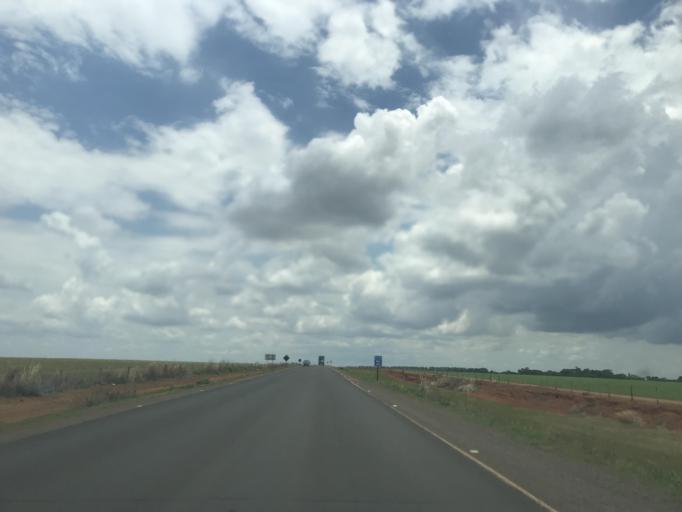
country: BR
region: Goias
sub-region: Vianopolis
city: Vianopolis
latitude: -16.7745
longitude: -48.5230
